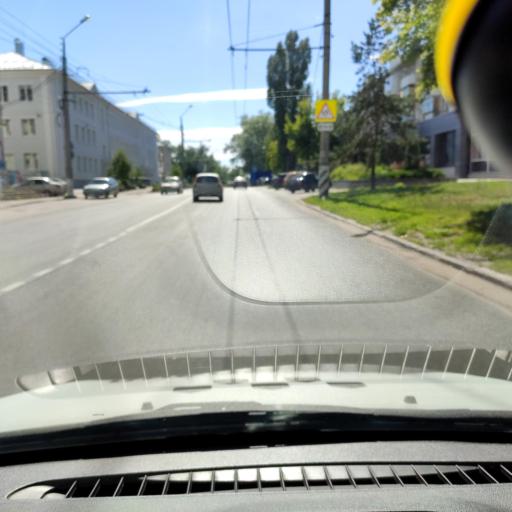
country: RU
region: Samara
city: Tol'yatti
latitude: 53.4782
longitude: 49.3696
